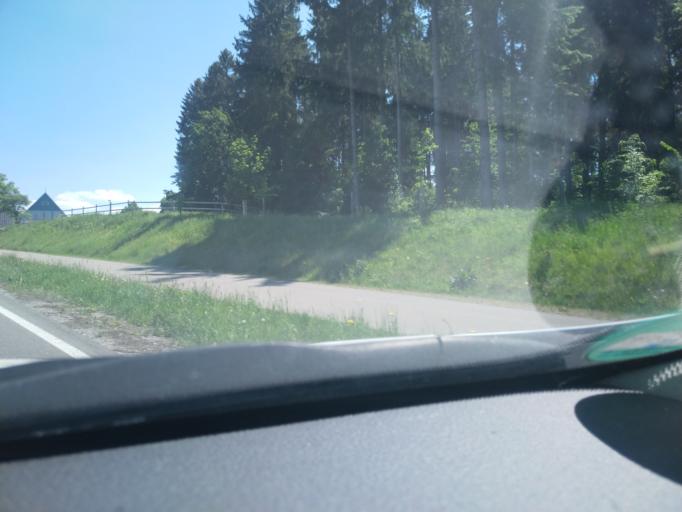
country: DE
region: Baden-Wuerttemberg
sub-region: Freiburg Region
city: Bosingen
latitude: 48.2017
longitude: 8.5473
